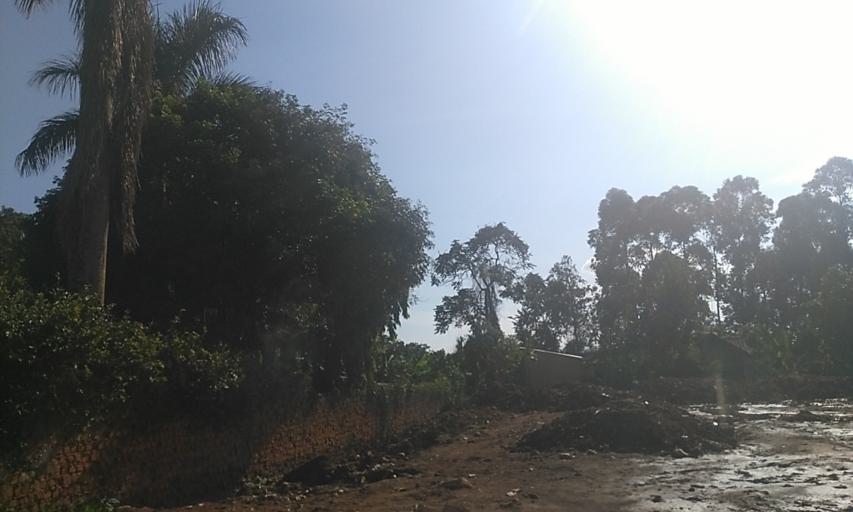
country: UG
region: Central Region
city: Kampala Central Division
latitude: 0.3226
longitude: 32.5429
